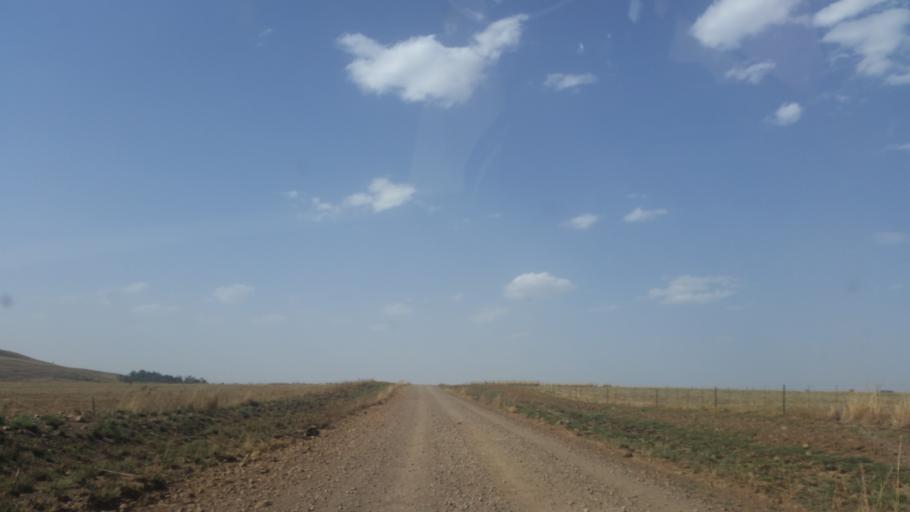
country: ZA
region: Orange Free State
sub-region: Thabo Mofutsanyana District Municipality
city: Phuthaditjhaba
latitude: -28.2534
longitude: 28.6583
